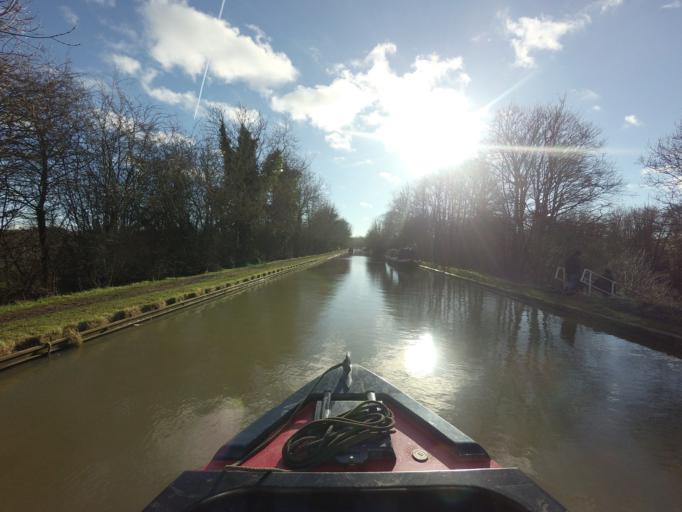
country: GB
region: England
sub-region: Northamptonshire
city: Bugbrooke
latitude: 52.2283
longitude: -1.0734
